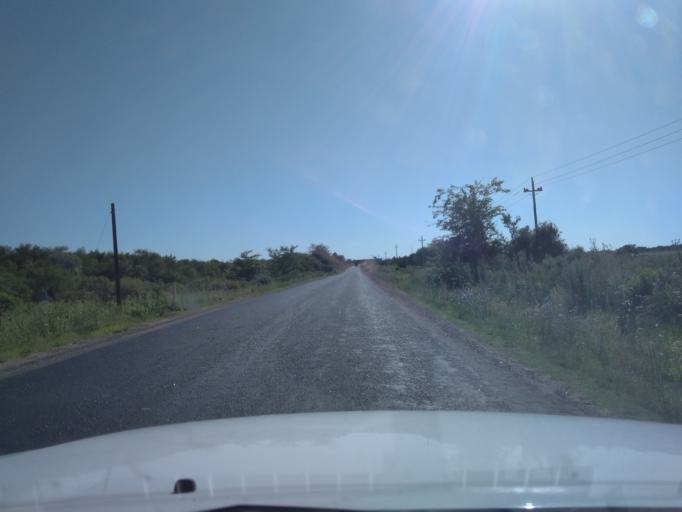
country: UY
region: Canelones
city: San Ramon
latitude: -34.2692
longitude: -55.9391
